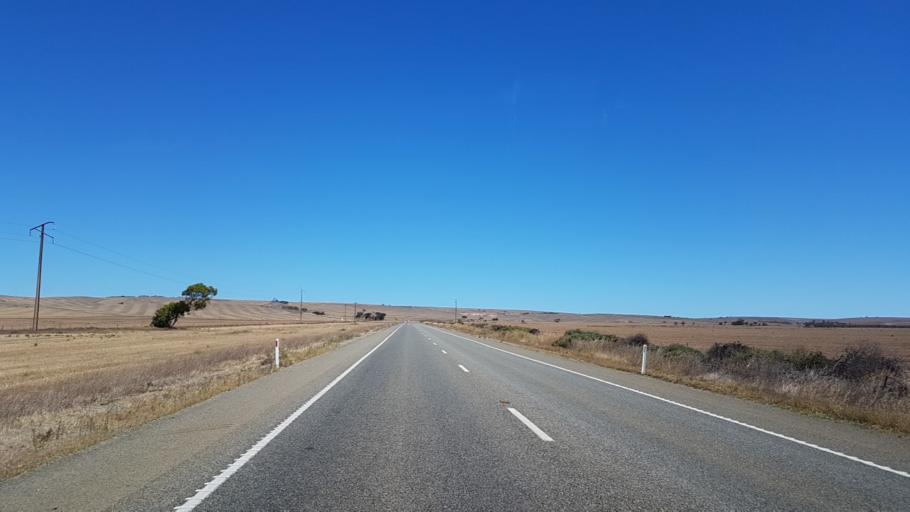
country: AU
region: South Australia
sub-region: Wakefield
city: Balaklava
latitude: -34.0771
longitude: 138.0775
